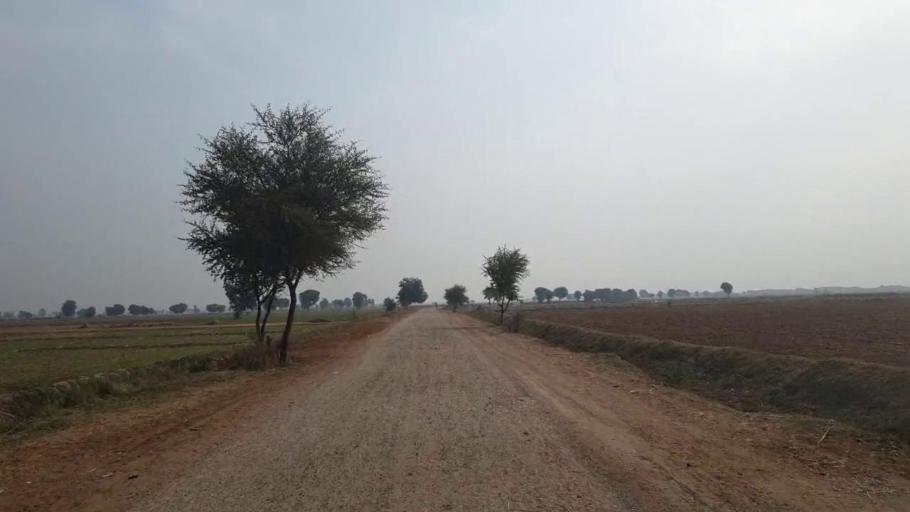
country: PK
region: Sindh
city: Sann
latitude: 26.0260
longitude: 68.1413
